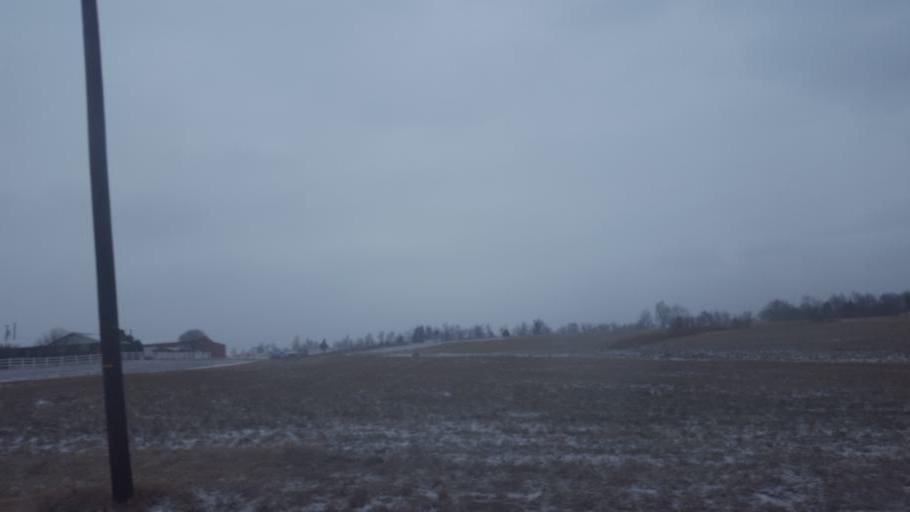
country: US
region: Kentucky
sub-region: Crittenden County
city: Marion
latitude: 37.3530
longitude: -88.0557
